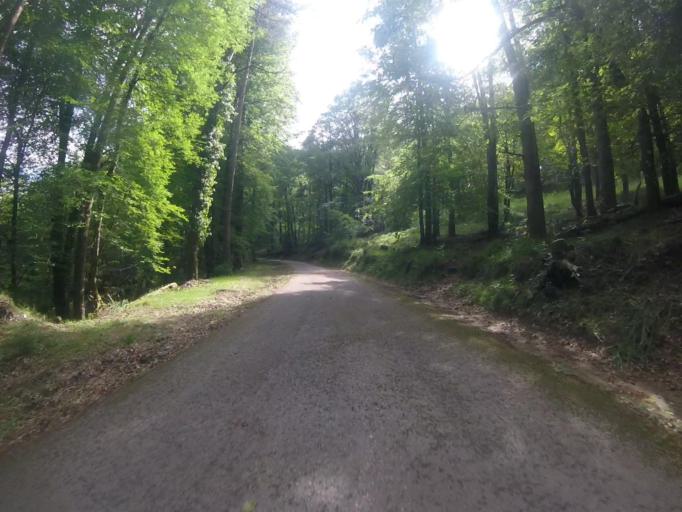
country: ES
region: Navarre
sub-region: Provincia de Navarra
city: Goizueta
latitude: 43.2315
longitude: -1.8063
